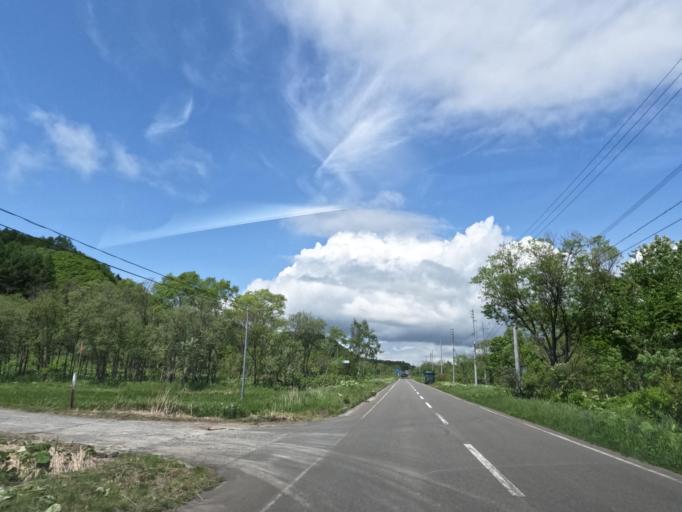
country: JP
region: Hokkaido
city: Tobetsu
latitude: 43.3930
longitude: 141.5795
